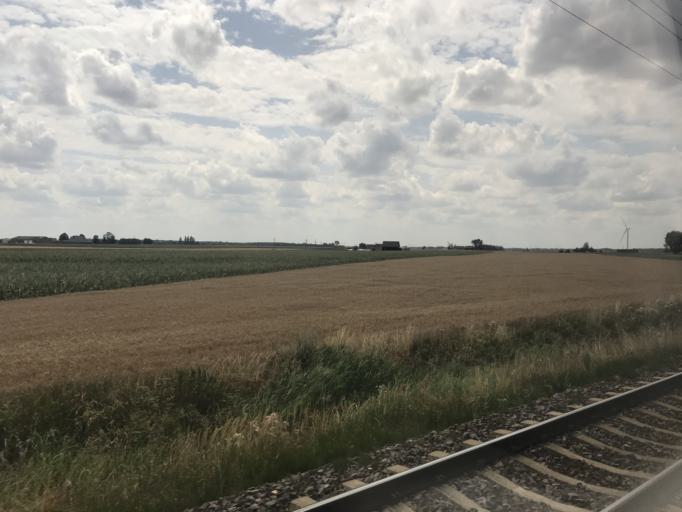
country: PL
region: Greater Poland Voivodeship
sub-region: Powiat poznanski
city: Buk
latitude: 52.3366
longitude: 16.4980
